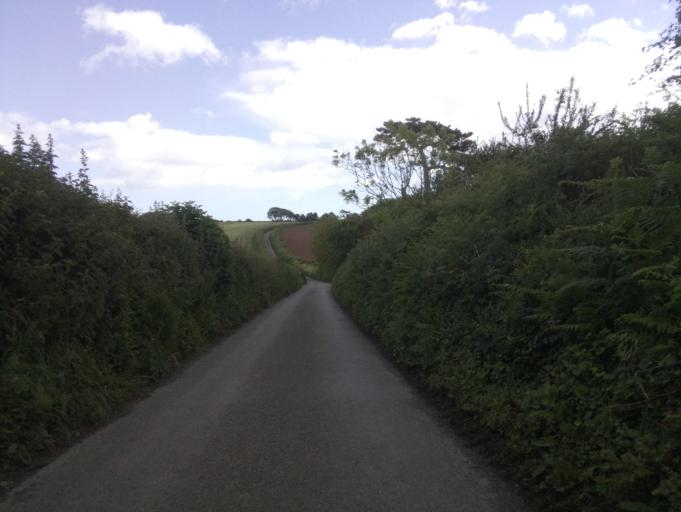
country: GB
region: England
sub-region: Devon
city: Dartmouth
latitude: 50.3547
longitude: -3.5401
